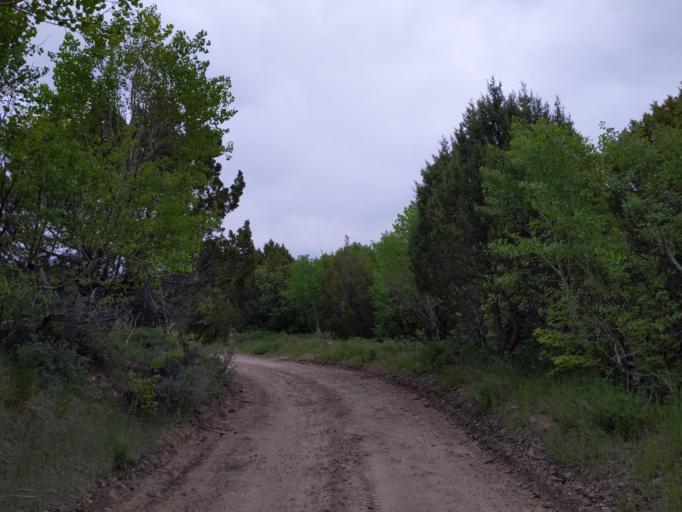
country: US
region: Idaho
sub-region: Bannock County
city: Pocatello
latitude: 42.8335
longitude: -112.4764
